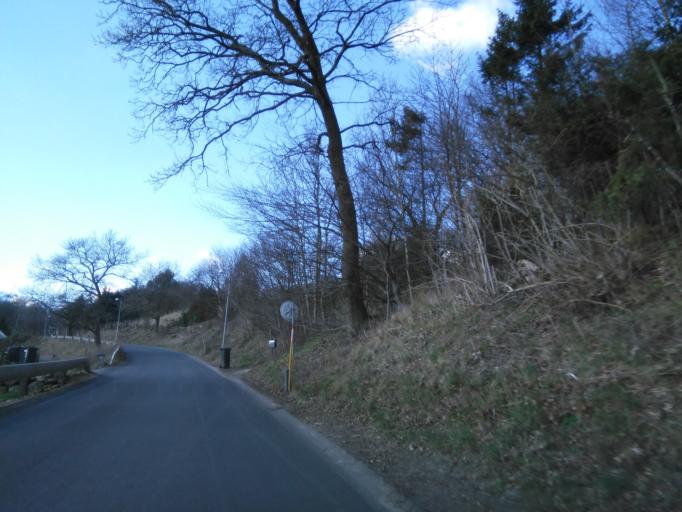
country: DK
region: Central Jutland
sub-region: Skanderborg Kommune
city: Ry
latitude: 56.1271
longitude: 9.7230
